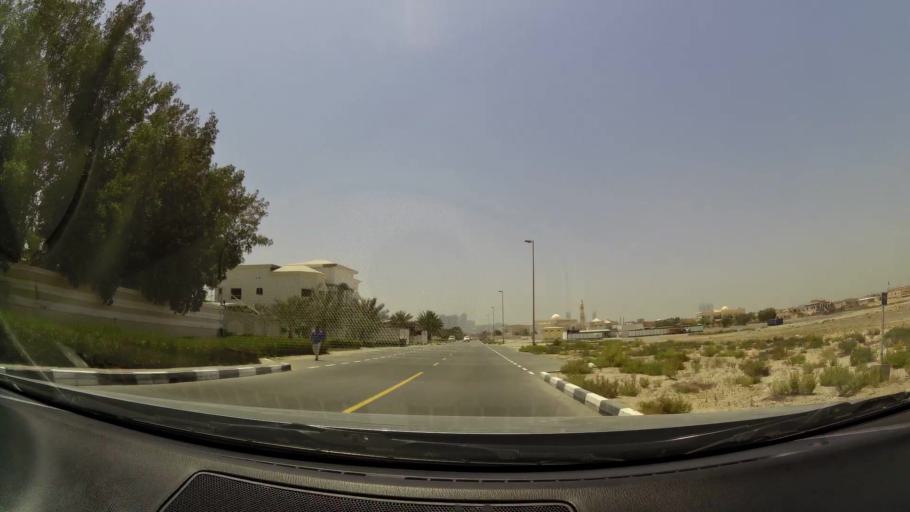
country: AE
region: Dubai
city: Dubai
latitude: 25.0853
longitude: 55.2057
